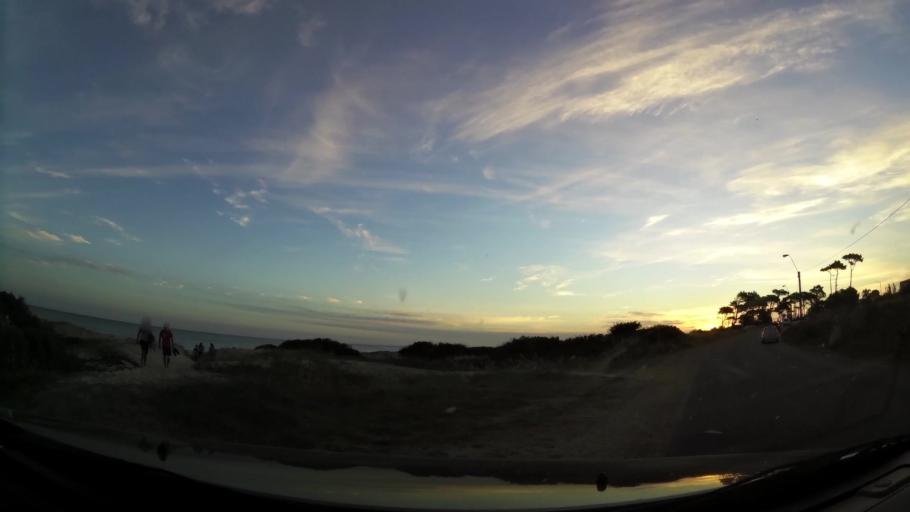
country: UY
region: Canelones
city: Atlantida
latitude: -34.7769
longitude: -55.7436
